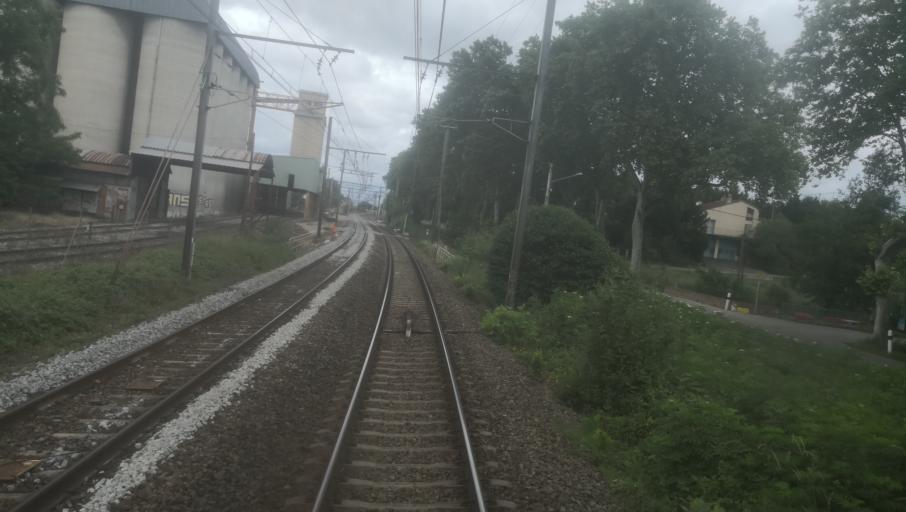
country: FR
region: Midi-Pyrenees
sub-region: Departement de la Haute-Garonne
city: Baziege
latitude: 43.4516
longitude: 1.6260
